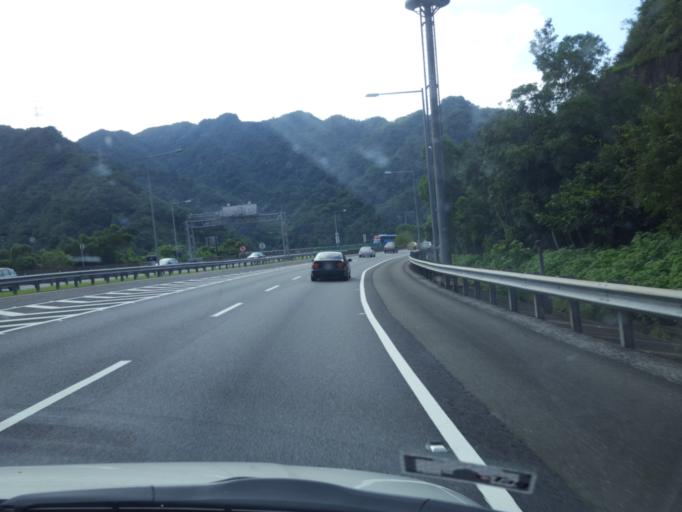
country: TW
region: Taipei
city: Taipei
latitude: 24.9822
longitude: 121.6638
